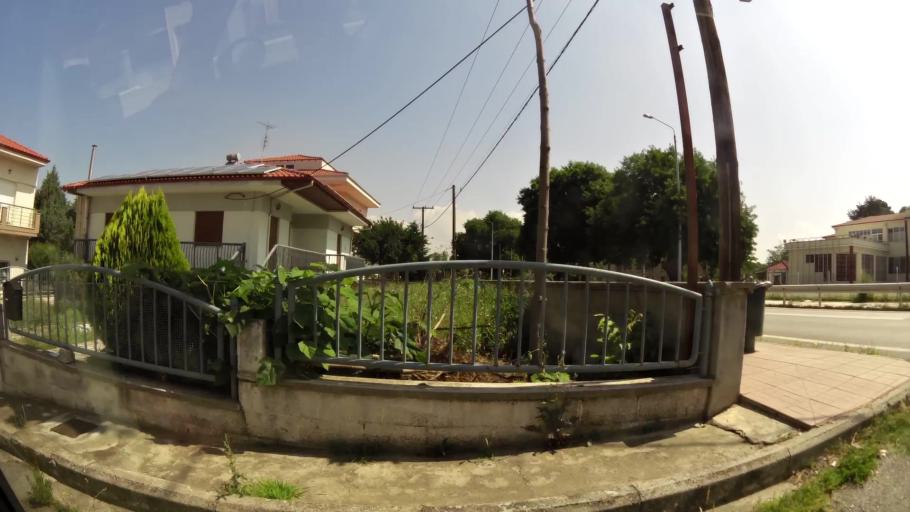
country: GR
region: West Macedonia
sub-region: Nomos Kozanis
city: Koila
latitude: 40.3323
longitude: 21.7900
